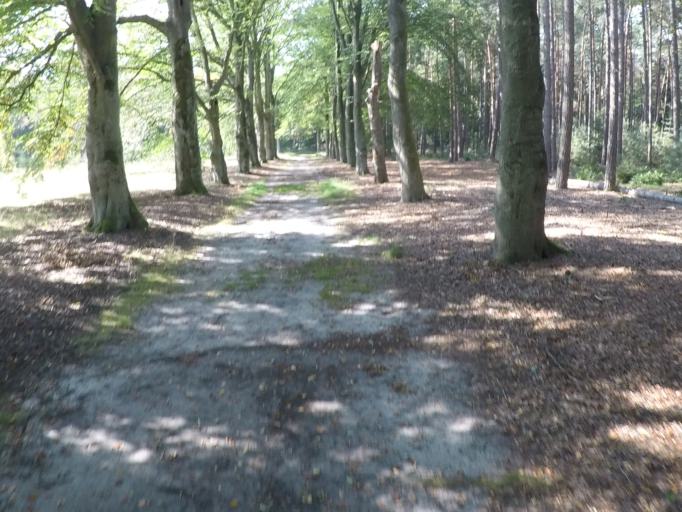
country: BE
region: Flanders
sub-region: Provincie Antwerpen
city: Kapellen
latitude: 51.3414
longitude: 4.4378
